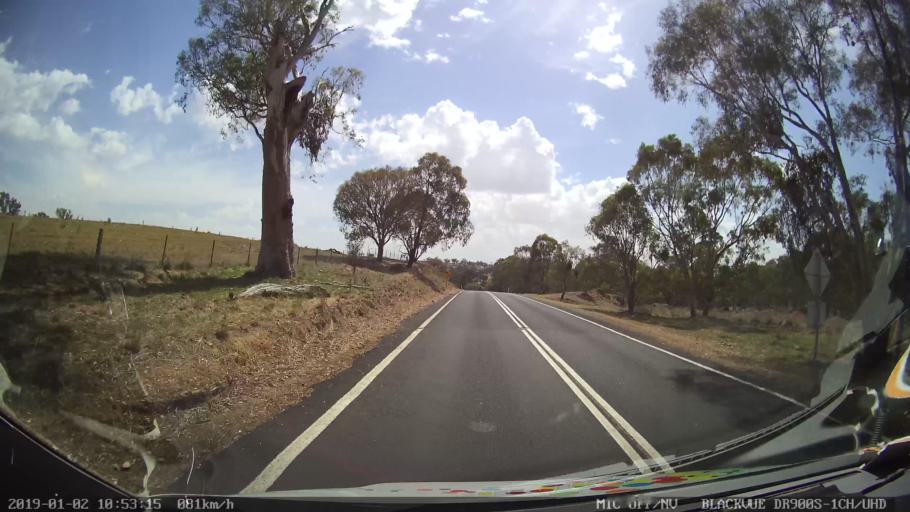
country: AU
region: New South Wales
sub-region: Cootamundra
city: Cootamundra
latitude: -34.6797
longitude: 148.2740
